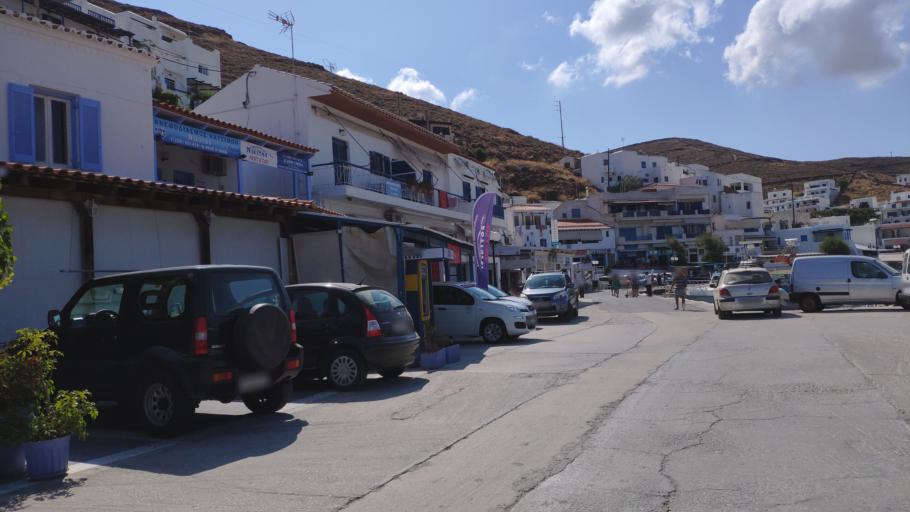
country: GR
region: South Aegean
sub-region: Nomos Kykladon
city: Kythnos
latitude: 37.3902
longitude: 24.3973
